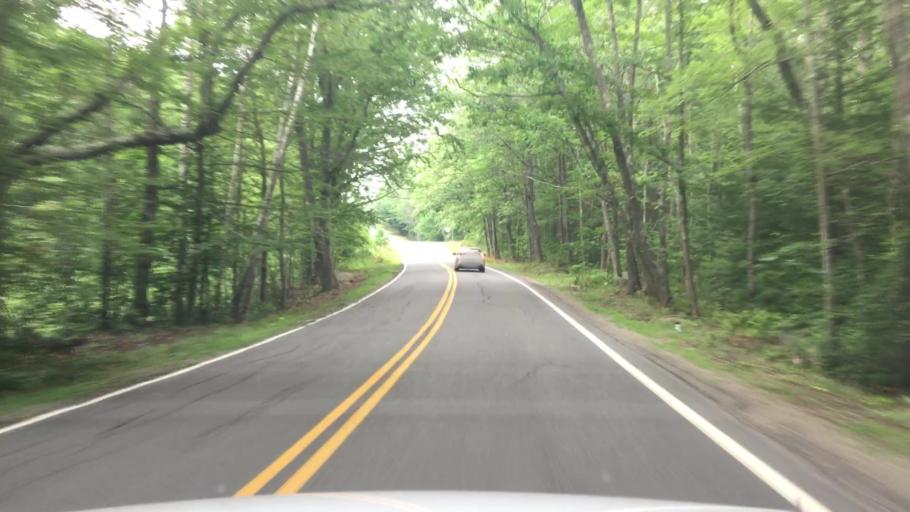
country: US
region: Maine
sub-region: Knox County
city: Washington
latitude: 44.2925
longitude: -69.3622
